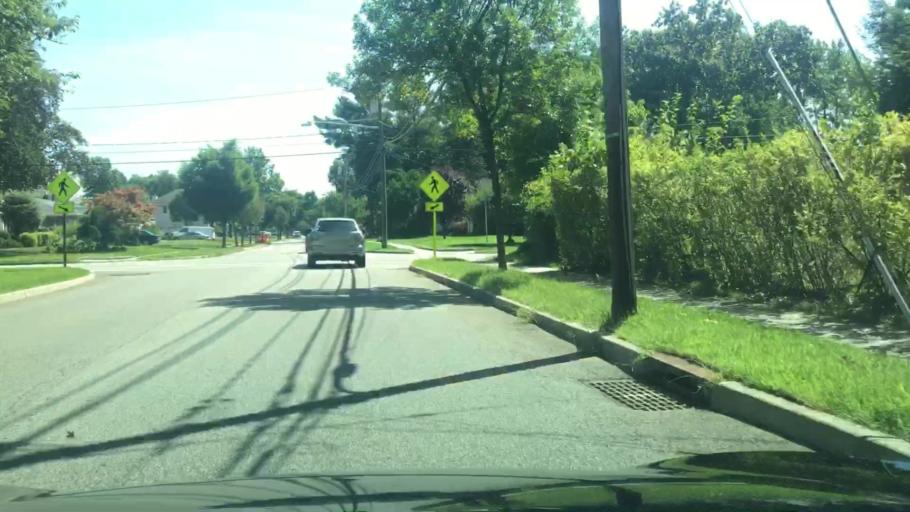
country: US
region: New Jersey
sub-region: Bergen County
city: River Edge
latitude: 40.9221
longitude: -74.0482
